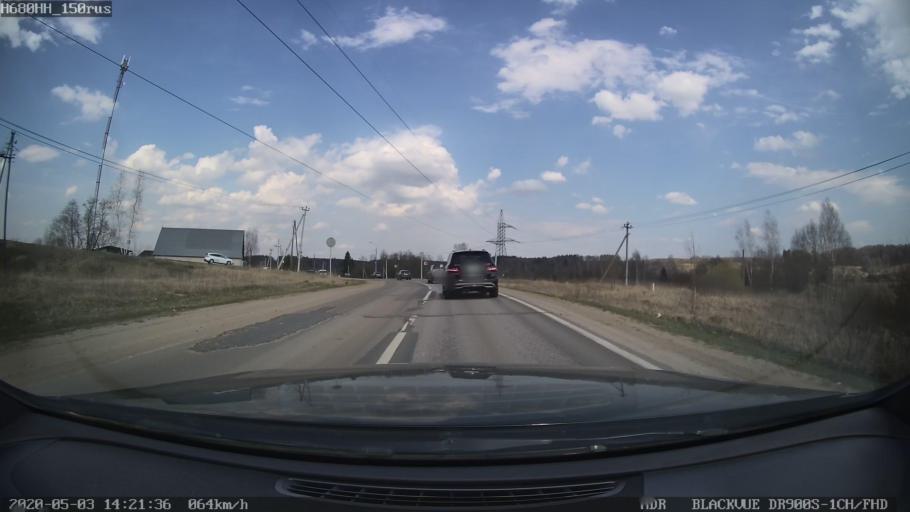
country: RU
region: Moskovskaya
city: Solnechnogorsk
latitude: 56.2562
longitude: 36.9815
